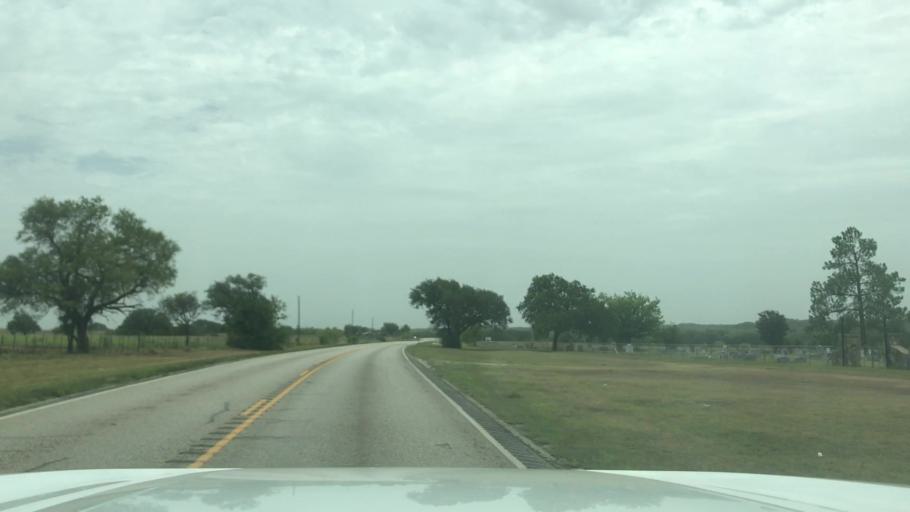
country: US
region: Texas
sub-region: Hamilton County
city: Hico
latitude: 32.0449
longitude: -98.1418
